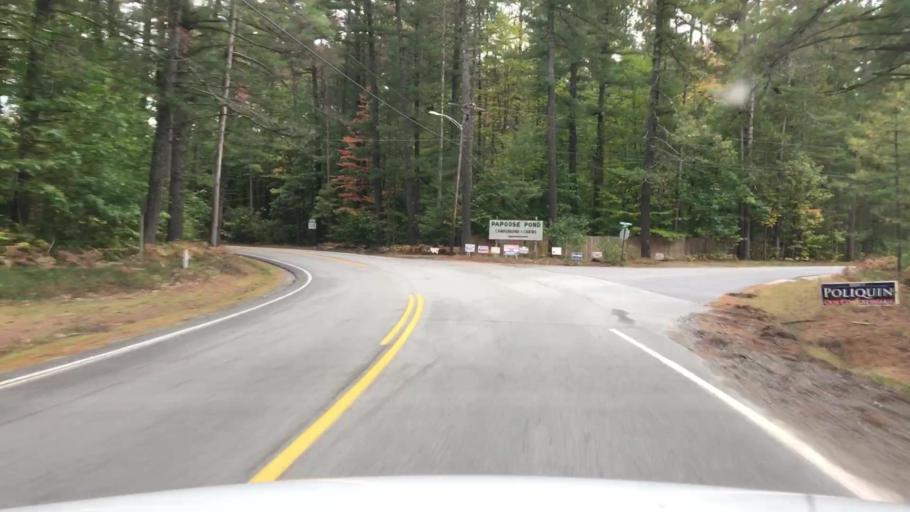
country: US
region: Maine
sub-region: Cumberland County
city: Harrison
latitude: 44.2292
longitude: -70.7047
